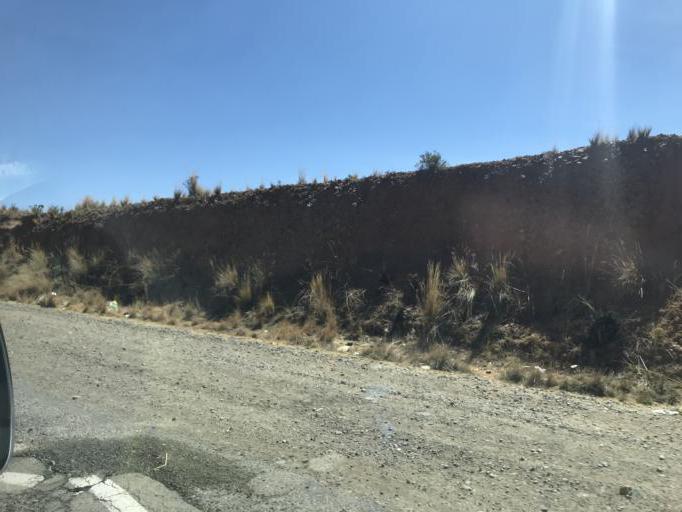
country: BO
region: La Paz
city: Tiahuanaco
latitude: -16.5801
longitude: -68.5300
